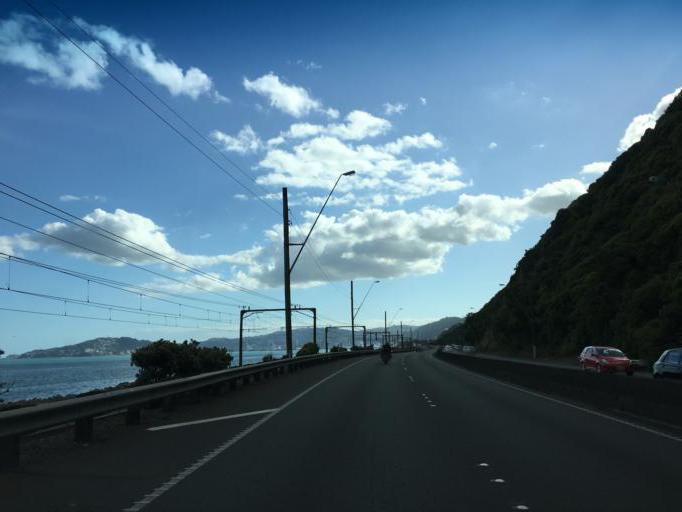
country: NZ
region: Wellington
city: Petone
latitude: -41.2396
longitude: 174.8270
